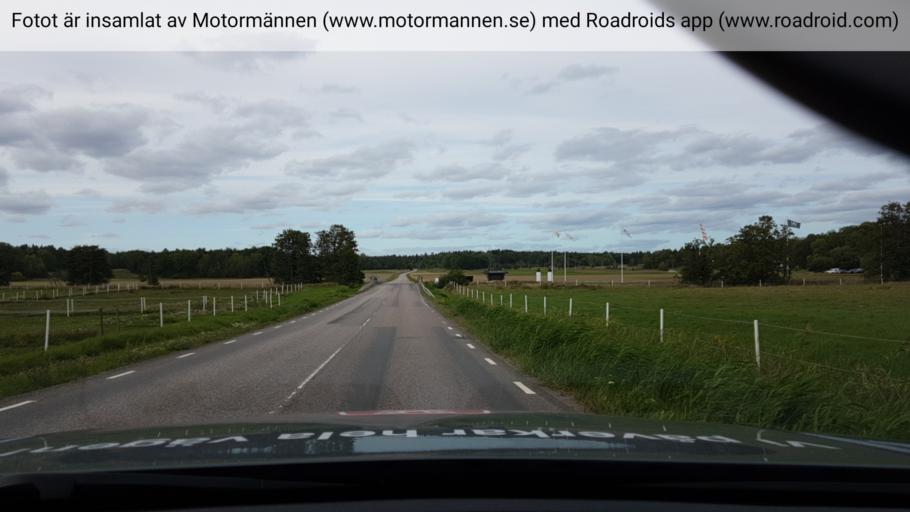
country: SE
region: Stockholm
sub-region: Haninge Kommun
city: Haninge
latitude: 59.1037
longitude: 18.1863
